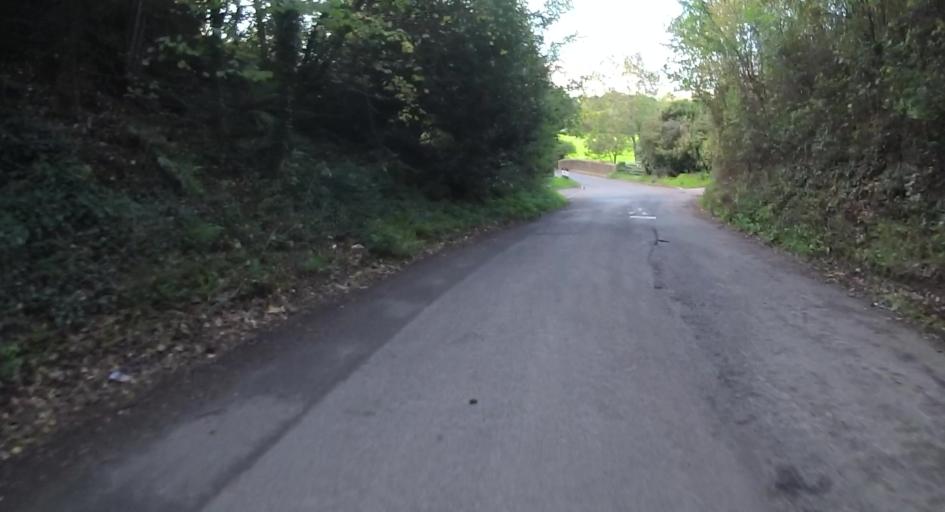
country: GB
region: England
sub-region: Surrey
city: Farnham
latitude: 51.2019
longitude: -0.8199
